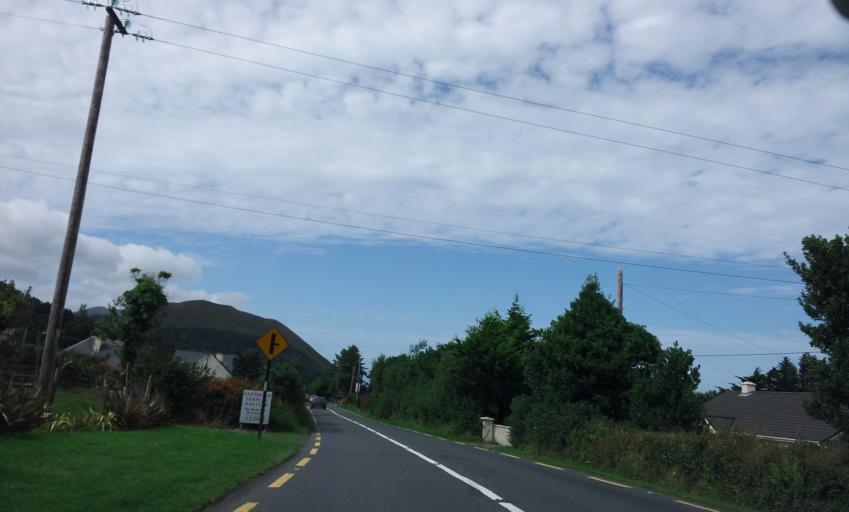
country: IE
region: Munster
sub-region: Ciarrai
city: Killorglin
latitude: 52.0595
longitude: -9.9256
